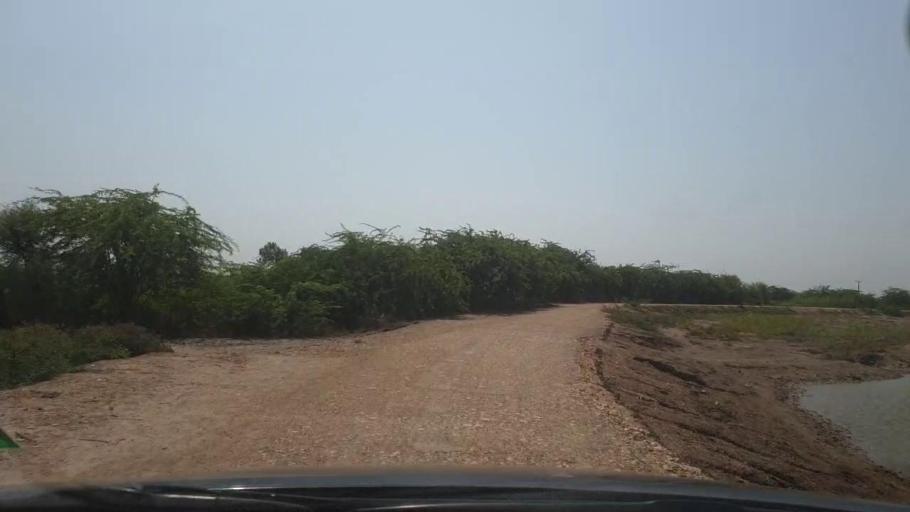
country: PK
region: Sindh
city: Tando Bago
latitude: 24.8049
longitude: 69.1556
